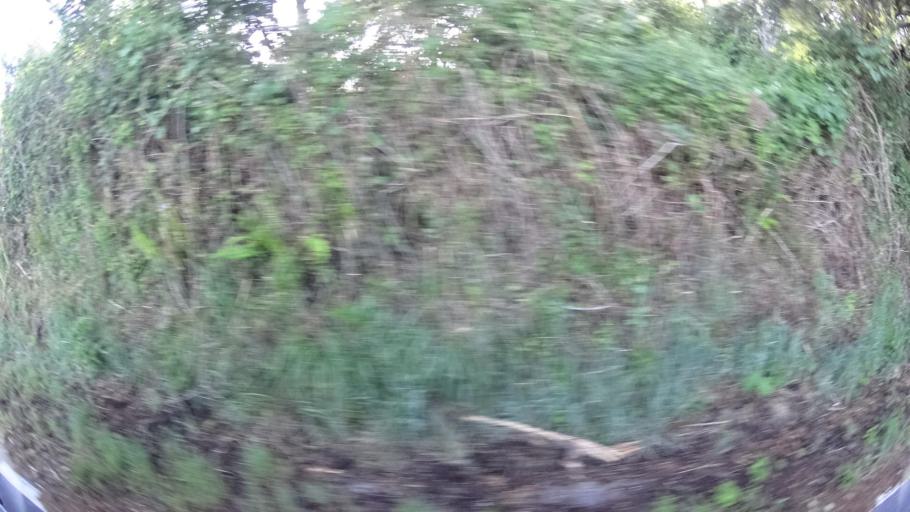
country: US
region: California
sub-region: Humboldt County
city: Westhaven-Moonstone
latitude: 41.0987
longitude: -124.1578
